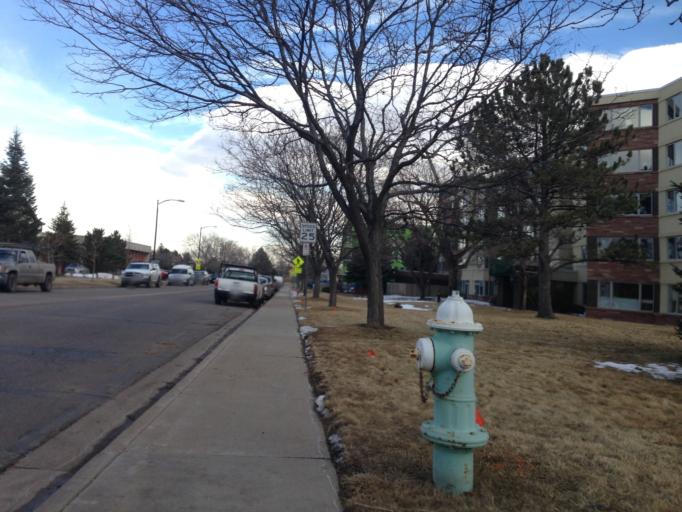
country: US
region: Colorado
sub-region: Boulder County
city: Boulder
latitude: 39.9956
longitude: -105.2347
